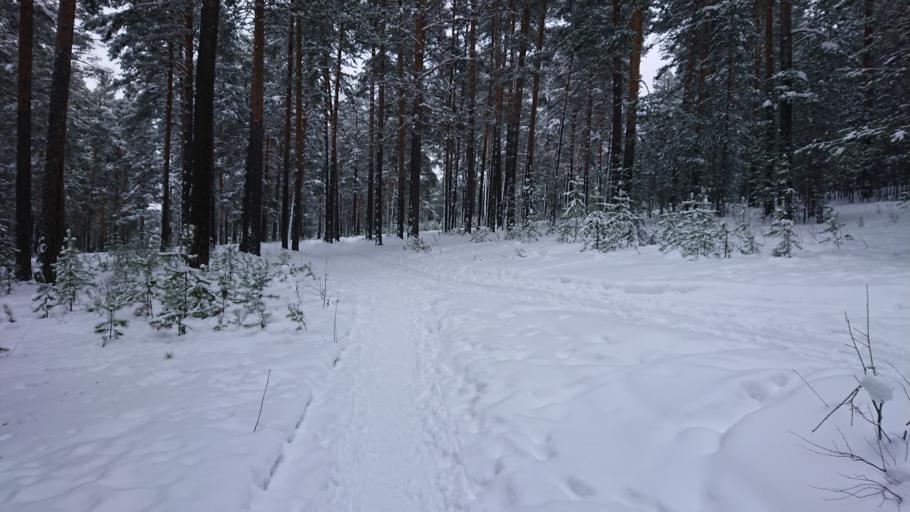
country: RU
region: Sverdlovsk
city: Degtyarsk
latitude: 56.6959
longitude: 60.0663
